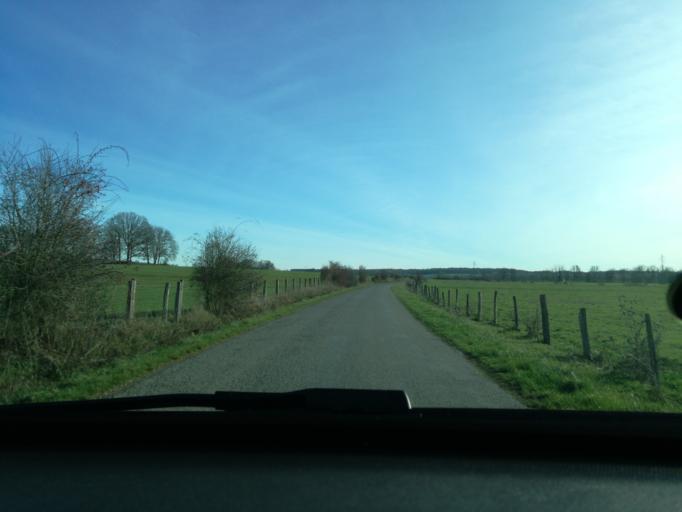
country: FR
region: Lorraine
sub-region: Departement de la Meuse
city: Revigny-sur-Ornain
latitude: 48.8217
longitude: 5.0540
